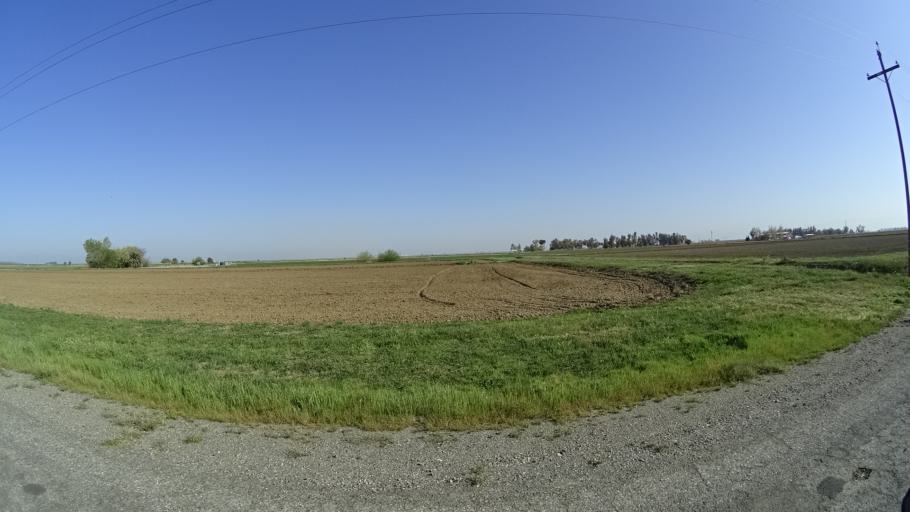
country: US
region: California
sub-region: Glenn County
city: Willows
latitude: 39.5747
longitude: -122.1105
